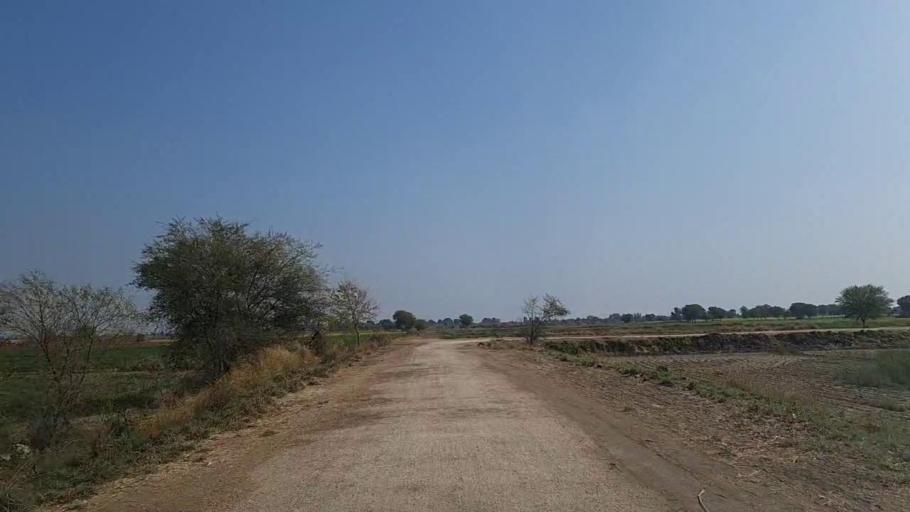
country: PK
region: Sindh
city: Nawabshah
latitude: 26.2532
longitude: 68.4914
